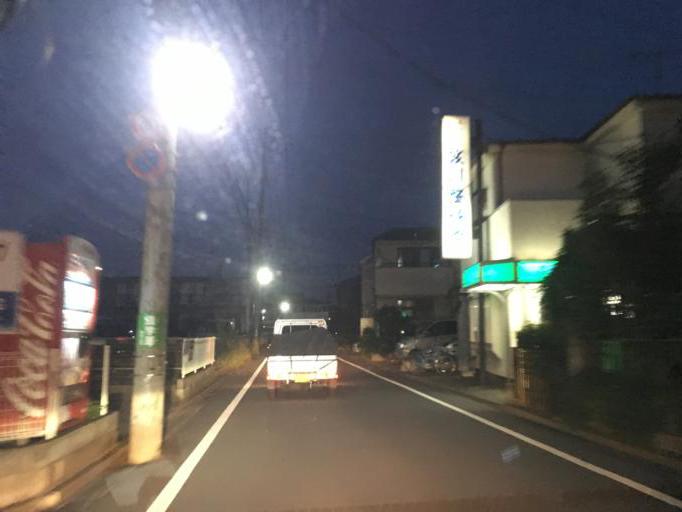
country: JP
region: Tokyo
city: Higashimurayama-shi
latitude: 35.7457
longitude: 139.4516
